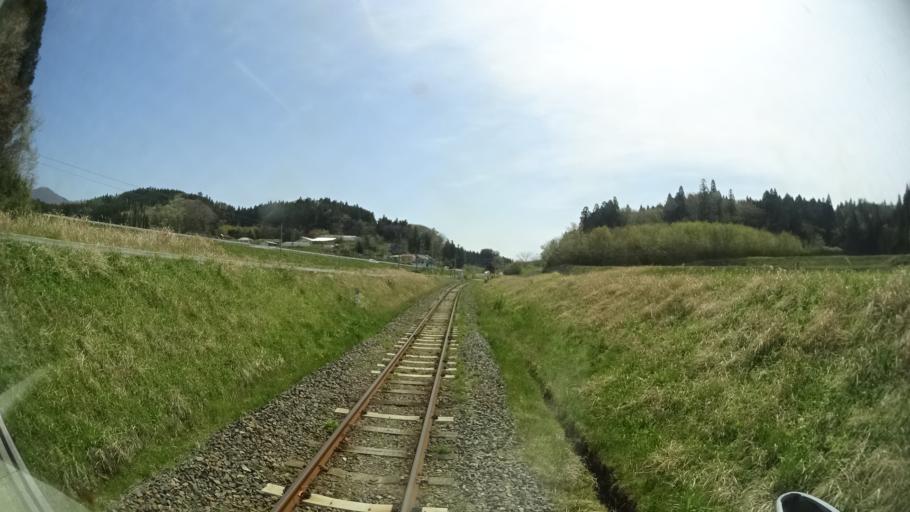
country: JP
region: Iwate
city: Ichinoseki
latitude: 38.9375
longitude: 141.4124
